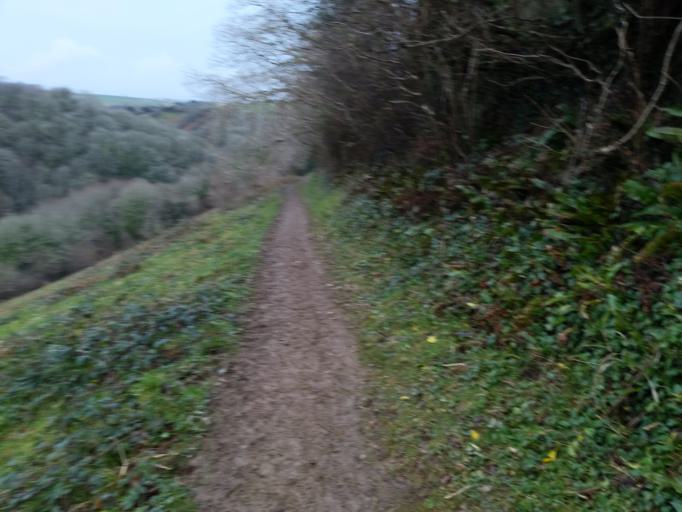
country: GB
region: England
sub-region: Cornwall
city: Fowey
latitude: 50.3351
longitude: -4.6134
